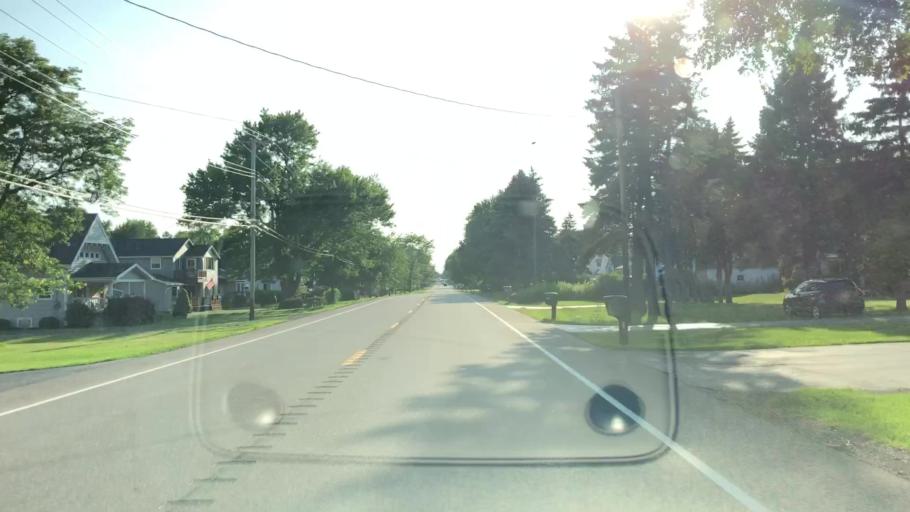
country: US
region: New York
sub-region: Erie County
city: Depew
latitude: 42.8578
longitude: -78.7216
